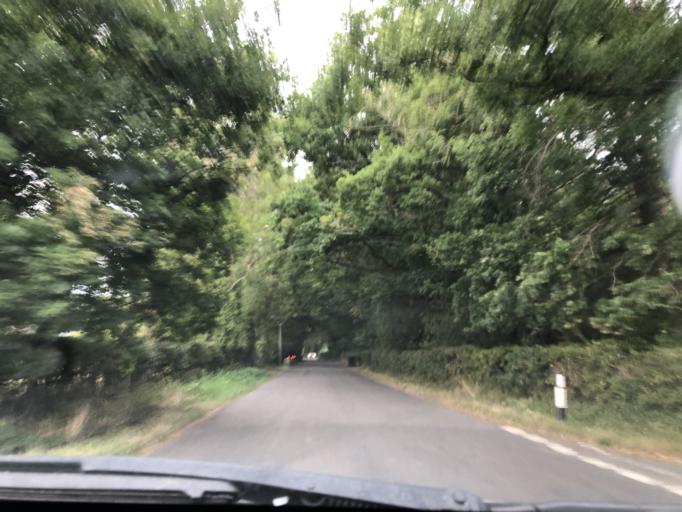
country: GB
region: England
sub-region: Kent
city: Tonbridge
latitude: 51.2293
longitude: 0.2353
